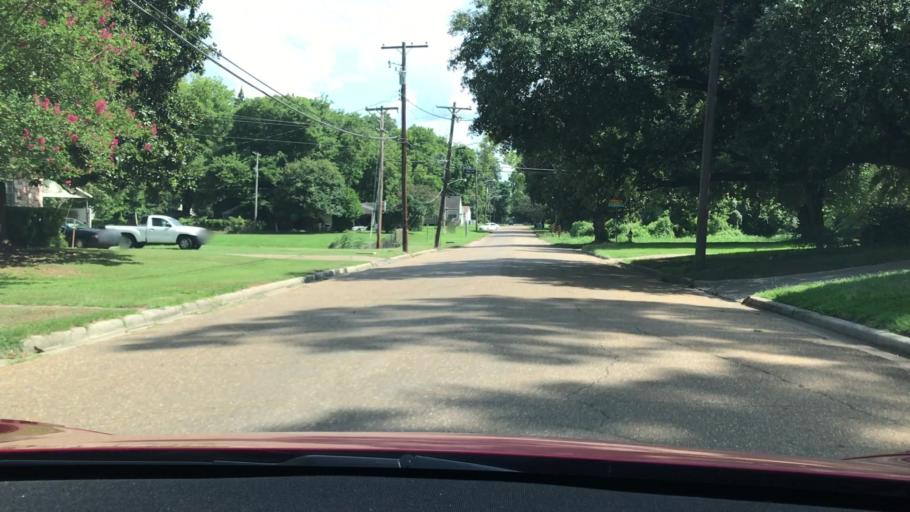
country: US
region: Louisiana
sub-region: Bossier Parish
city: Bossier City
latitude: 32.4787
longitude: -93.7312
